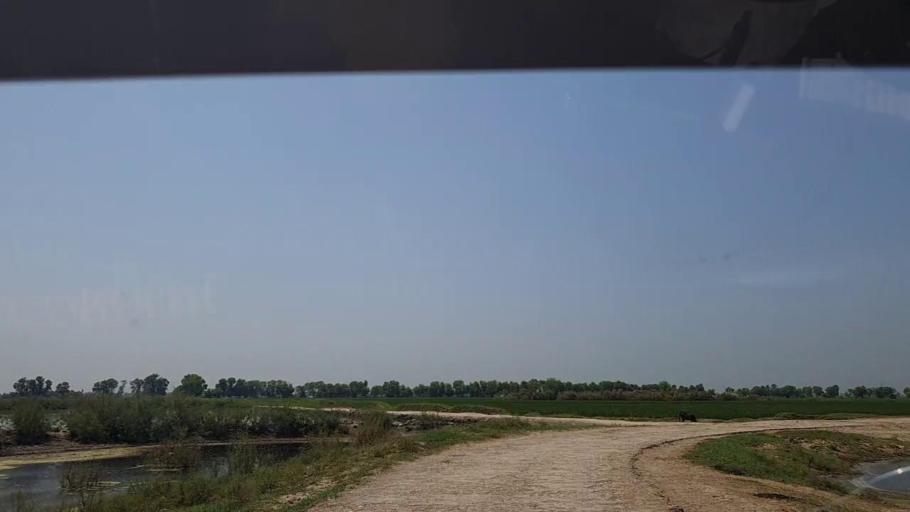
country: PK
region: Sindh
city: Ghauspur
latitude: 28.1863
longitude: 69.0938
